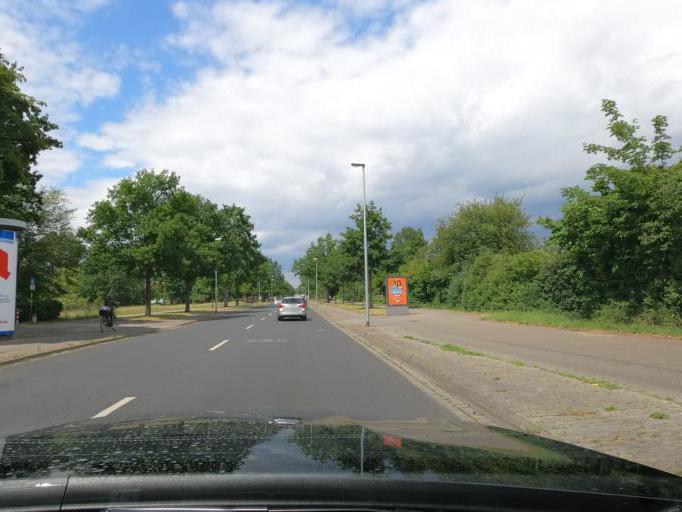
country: DE
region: Lower Saxony
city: Isernhagen Farster Bauerschaft
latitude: 52.3942
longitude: 9.8169
